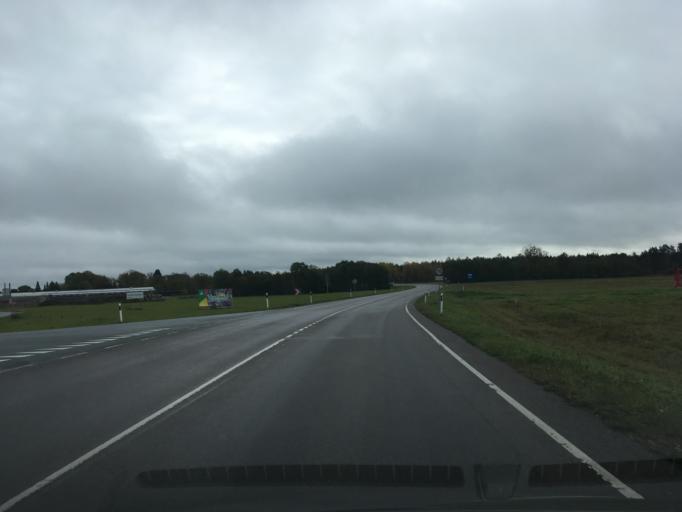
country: EE
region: Harju
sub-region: Saku vald
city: Saku
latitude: 59.3107
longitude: 24.6203
